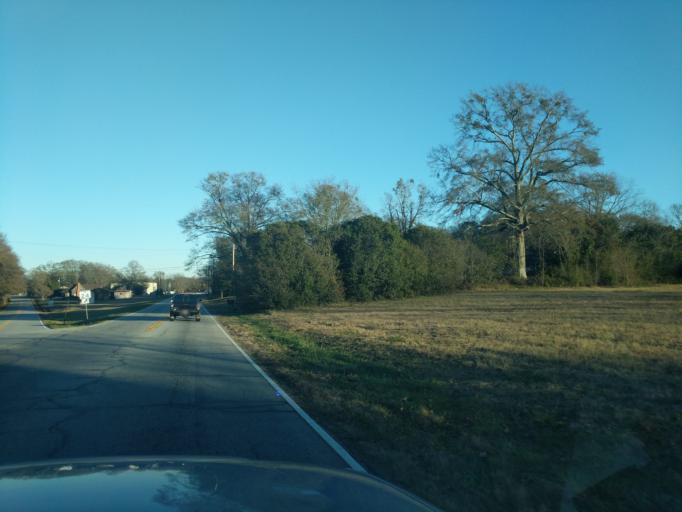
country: US
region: South Carolina
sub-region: Oconee County
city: Utica
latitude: 34.5650
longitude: -82.8936
